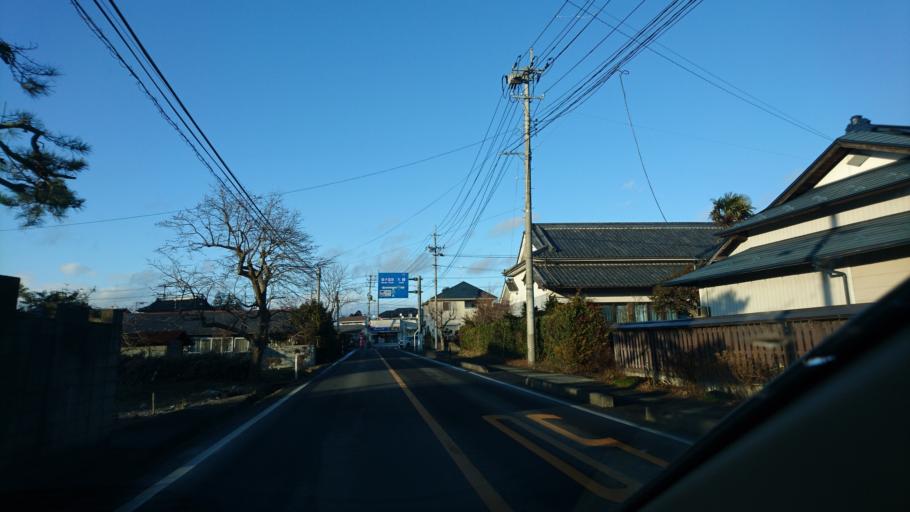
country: JP
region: Miyagi
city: Furukawa
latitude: 38.6475
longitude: 140.8697
